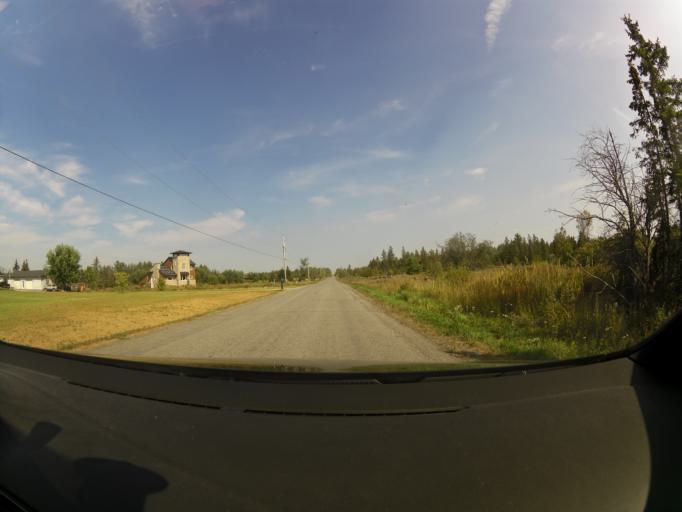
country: CA
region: Ontario
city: Carleton Place
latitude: 45.2980
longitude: -76.2192
